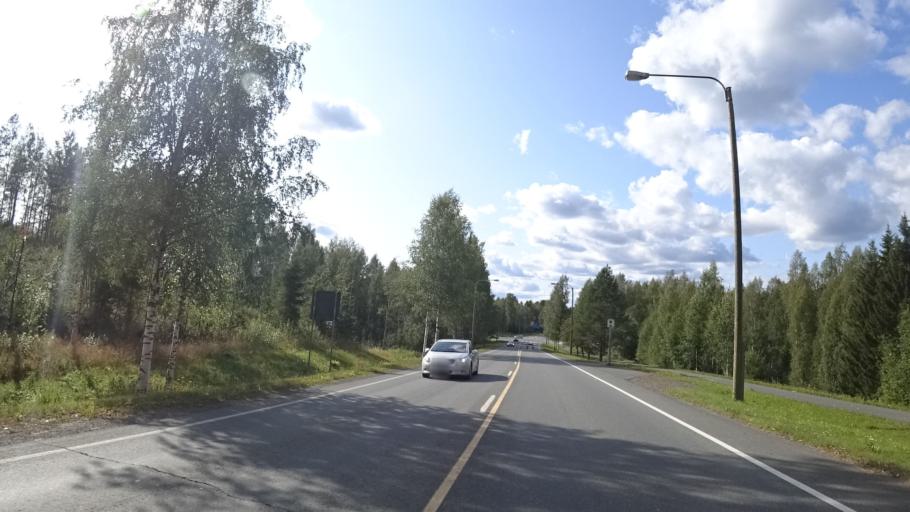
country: FI
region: North Karelia
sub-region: Keski-Karjala
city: Tohmajaervi
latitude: 62.2286
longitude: 30.3251
